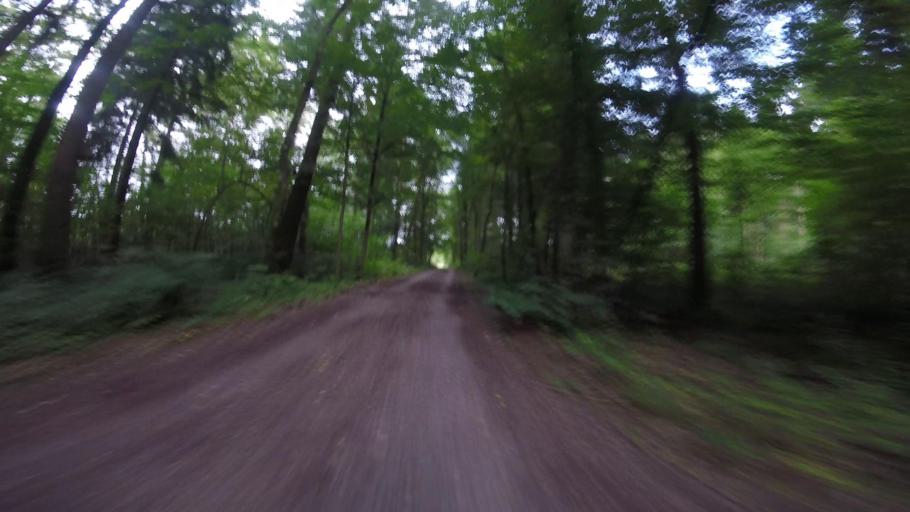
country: DE
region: Baden-Wuerttemberg
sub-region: Regierungsbezirk Stuttgart
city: Oberstenfeld
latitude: 48.9898
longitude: 9.3499
